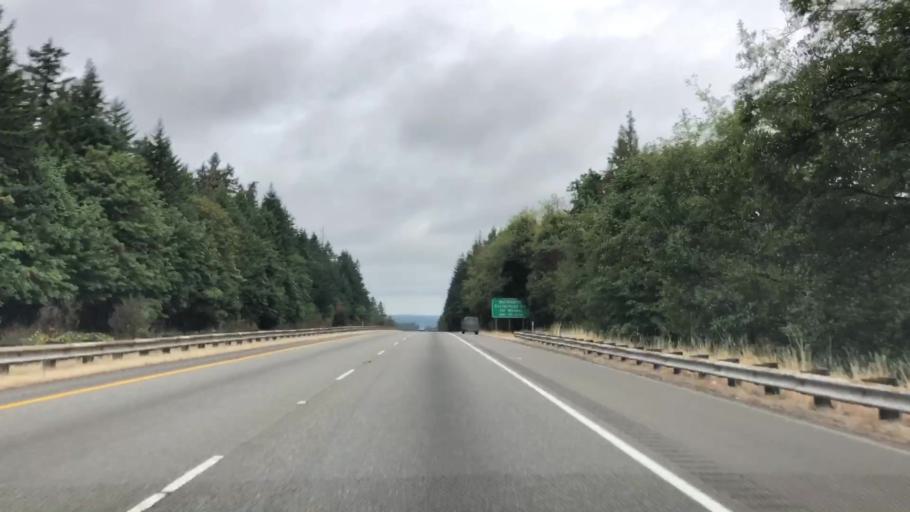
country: US
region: Washington
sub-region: Pierce County
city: Canterwood
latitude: 47.3476
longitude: -122.6096
